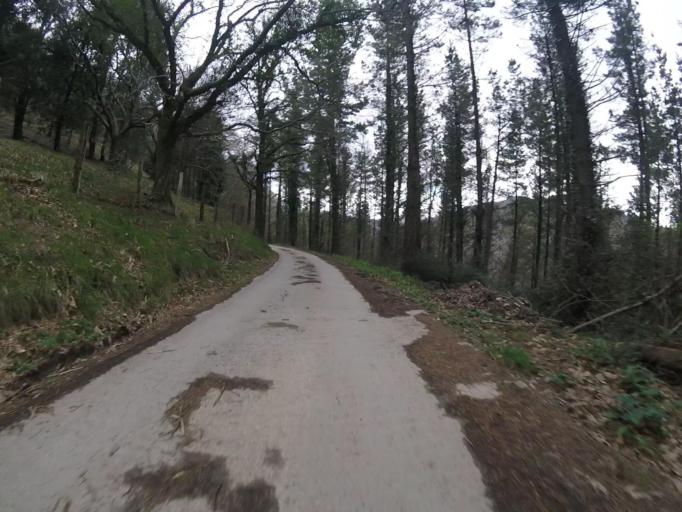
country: ES
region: Basque Country
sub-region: Provincia de Guipuzcoa
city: Errenteria
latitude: 43.2744
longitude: -1.8607
